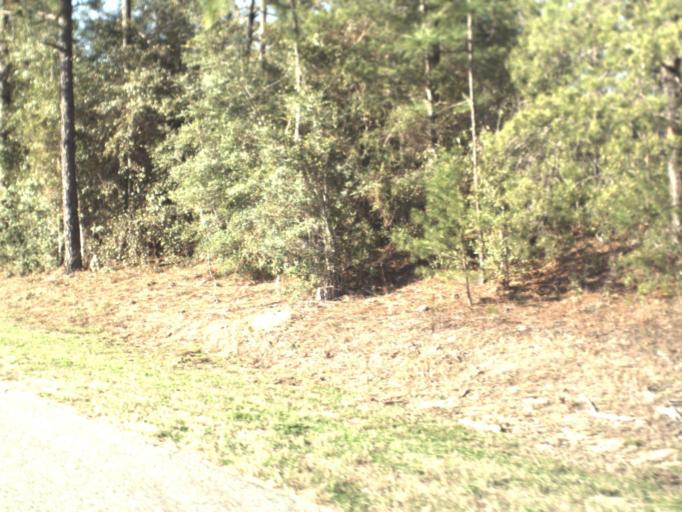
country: US
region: Florida
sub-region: Jackson County
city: Marianna
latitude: 30.6416
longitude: -85.1983
